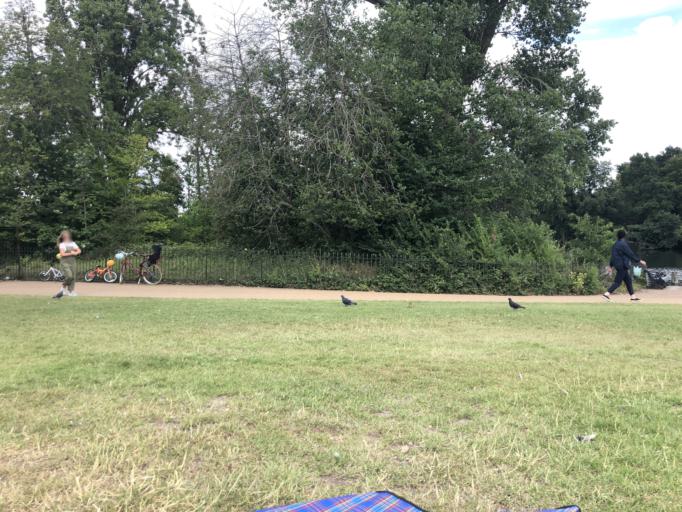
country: GB
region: England
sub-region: Greater London
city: Bayswater
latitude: 51.5075
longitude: -0.1753
